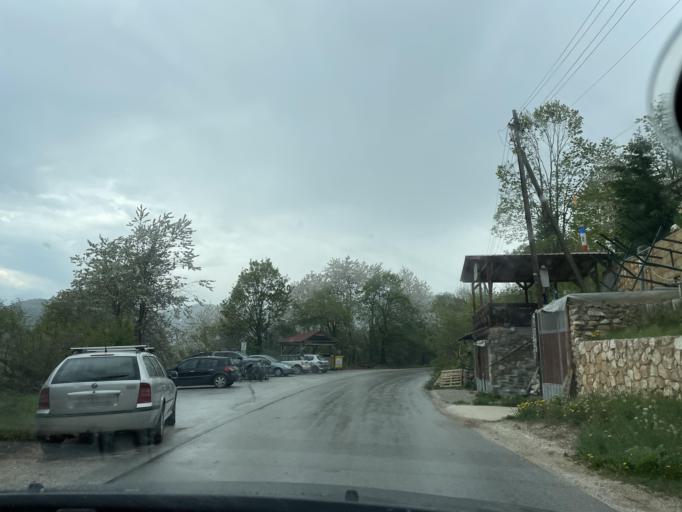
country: MK
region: Gostivar
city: Vrutok
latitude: 41.6830
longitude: 20.7390
